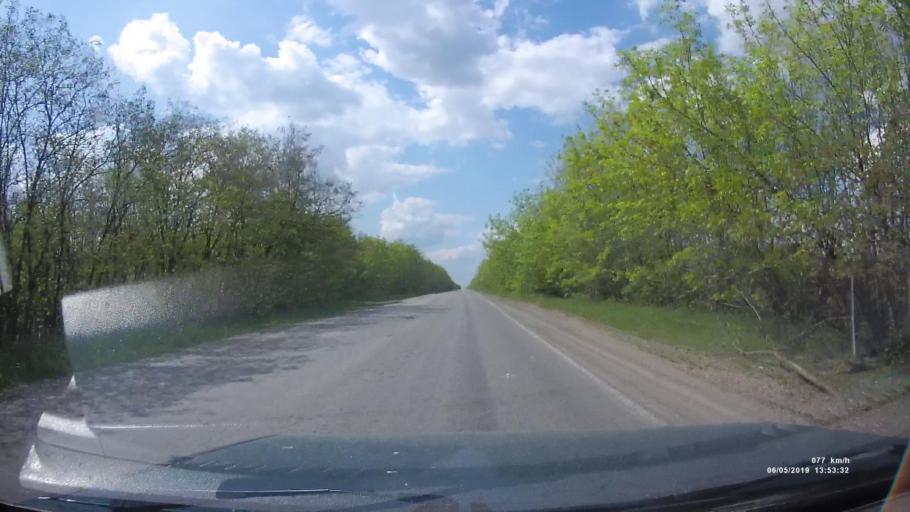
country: RU
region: Rostov
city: Melikhovskaya
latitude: 47.6688
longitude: 40.4611
